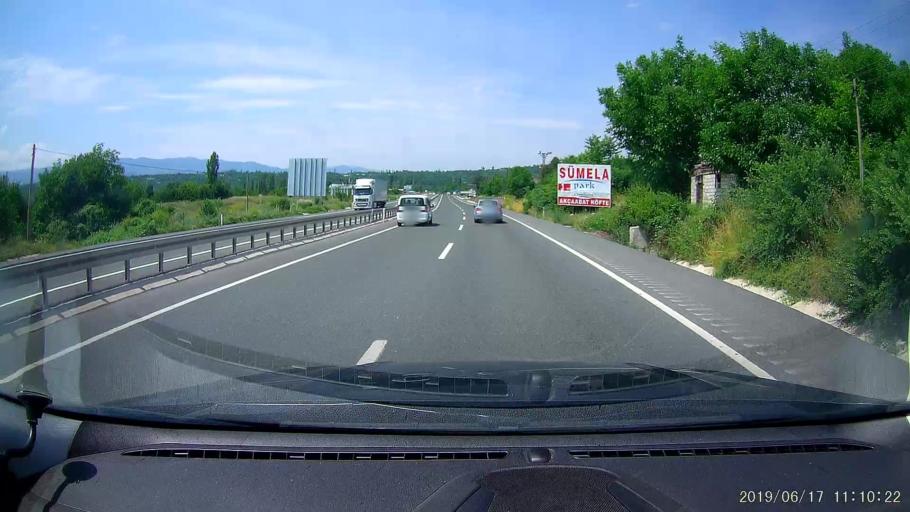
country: TR
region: Kastamonu
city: Tosya
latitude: 41.0001
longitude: 34.0255
